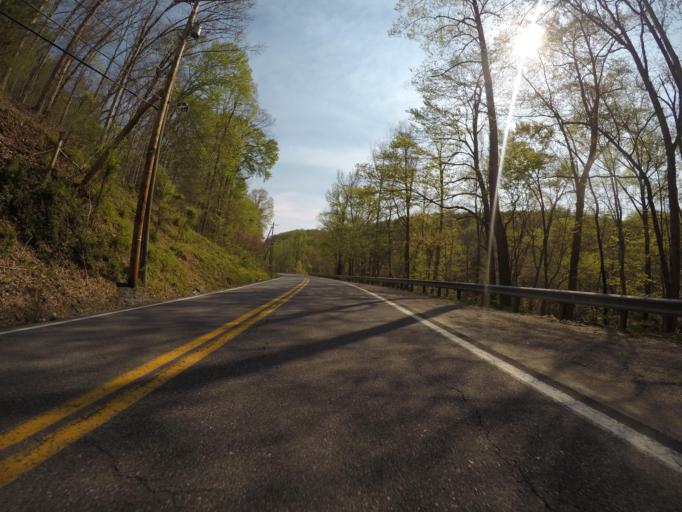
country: US
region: West Virginia
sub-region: Kanawha County
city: Pinch
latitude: 38.3915
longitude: -81.5581
